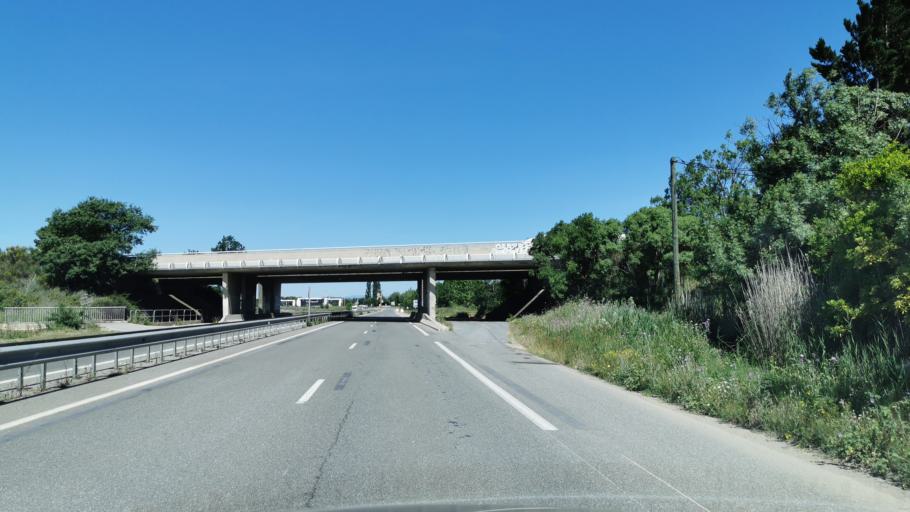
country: FR
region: Languedoc-Roussillon
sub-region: Departement de l'Aude
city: Narbonne
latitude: 43.1785
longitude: 3.0409
